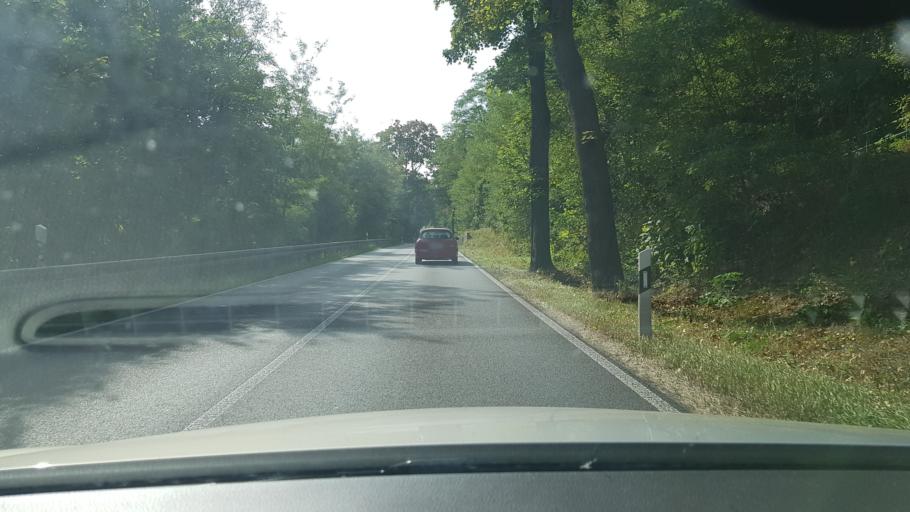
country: DE
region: Brandenburg
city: Lawitz
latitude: 52.1022
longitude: 14.6470
